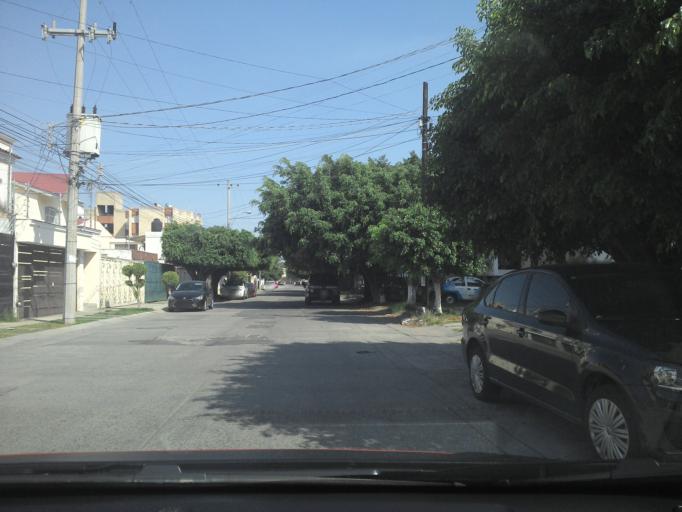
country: MX
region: Jalisco
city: Guadalajara
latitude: 20.6400
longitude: -103.4370
